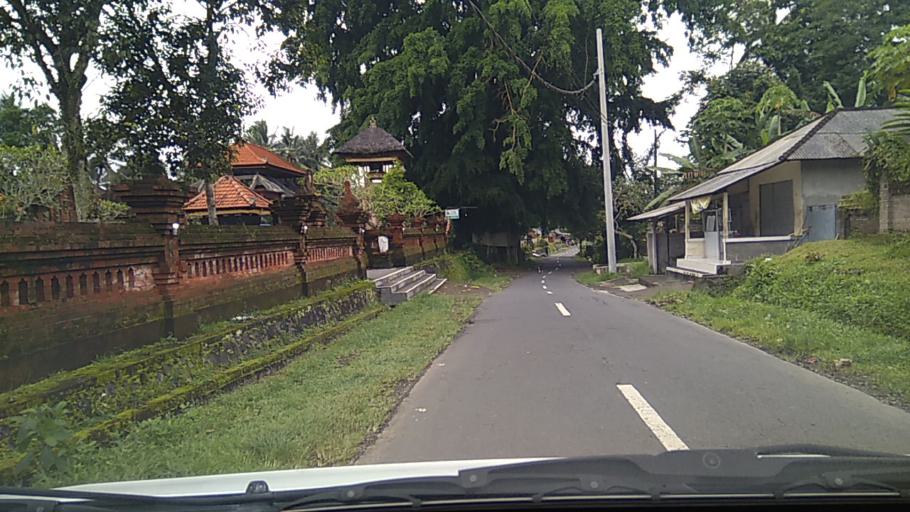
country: ID
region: Bali
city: Brahmana
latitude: -8.4789
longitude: 115.2010
